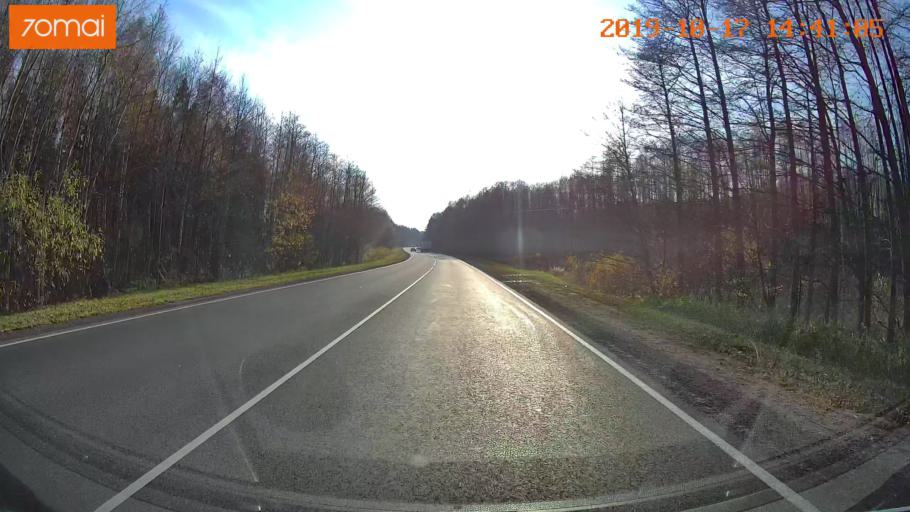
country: RU
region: Rjazan
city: Solotcha
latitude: 54.8494
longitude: 39.9440
